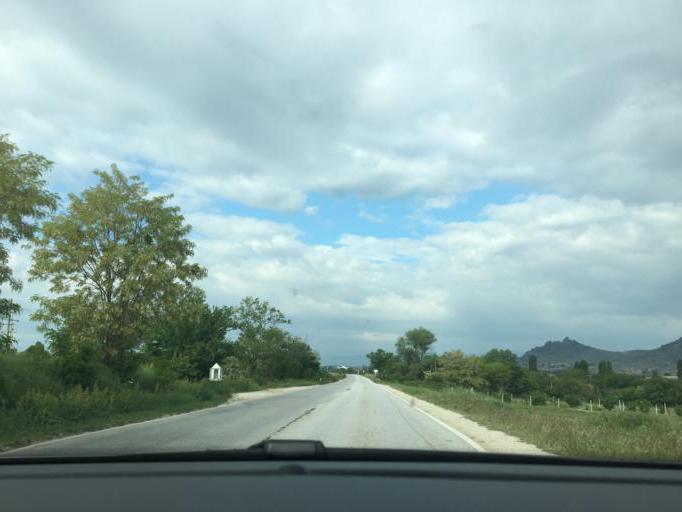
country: MK
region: Prilep
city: Prilep
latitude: 41.3620
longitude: 21.5990
